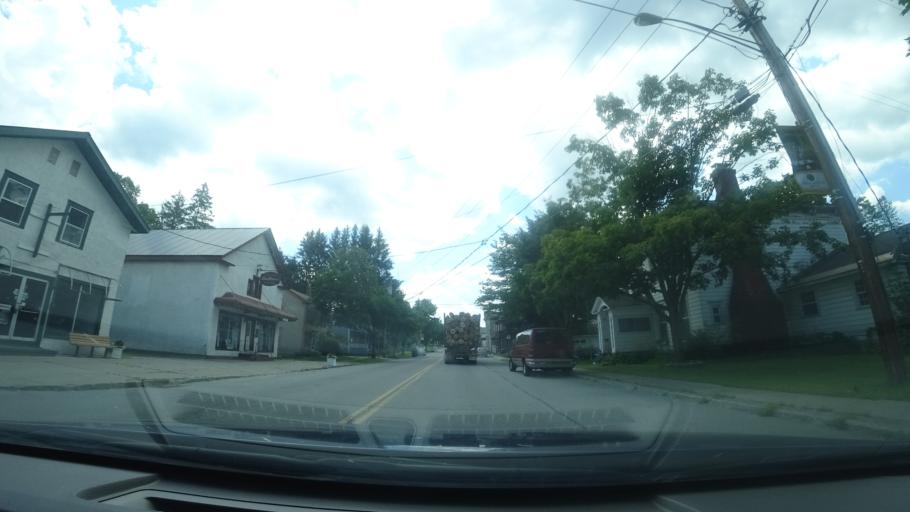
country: US
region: New York
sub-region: Warren County
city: Warrensburg
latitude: 43.6548
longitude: -73.8011
